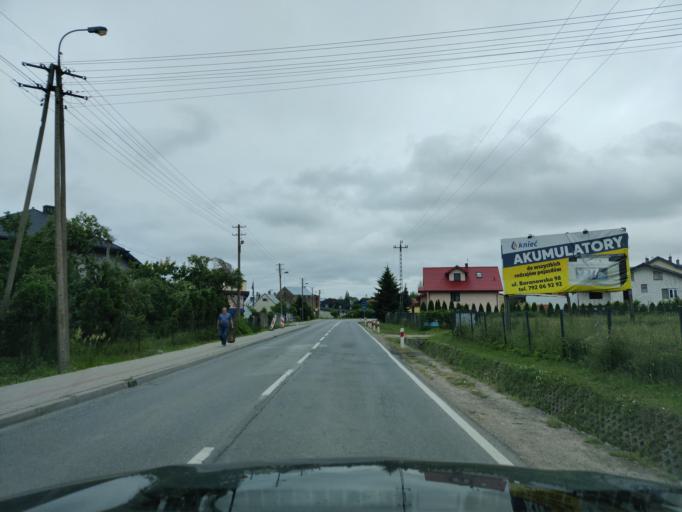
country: PL
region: Masovian Voivodeship
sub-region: Powiat przasnyski
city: Przasnysz
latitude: 53.0267
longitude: 20.8808
